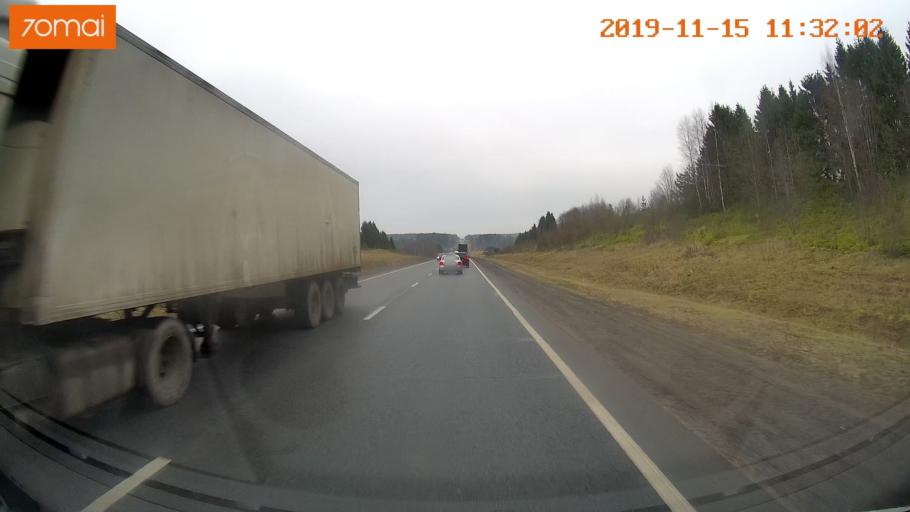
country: RU
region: Vologda
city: Molochnoye
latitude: 59.1839
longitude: 39.5660
